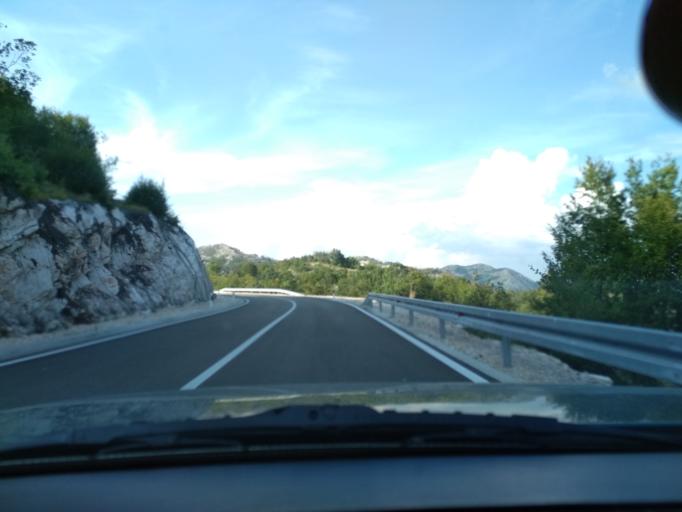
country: ME
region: Cetinje
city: Cetinje
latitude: 42.4227
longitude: 18.8744
